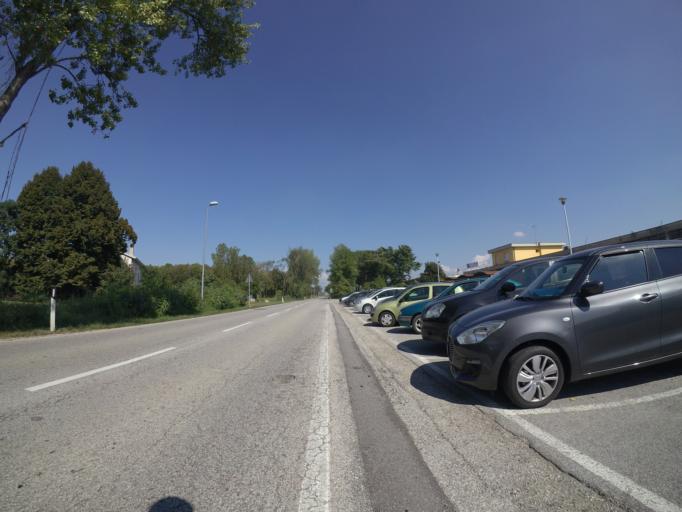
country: IT
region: Friuli Venezia Giulia
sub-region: Provincia di Udine
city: Codroipo
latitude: 45.9738
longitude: 12.9878
